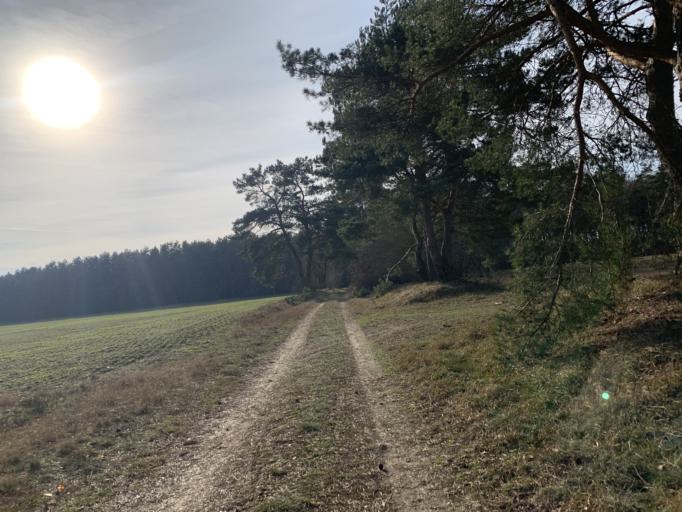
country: DE
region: Mecklenburg-Vorpommern
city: Wesenberg
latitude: 53.2883
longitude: 12.8649
